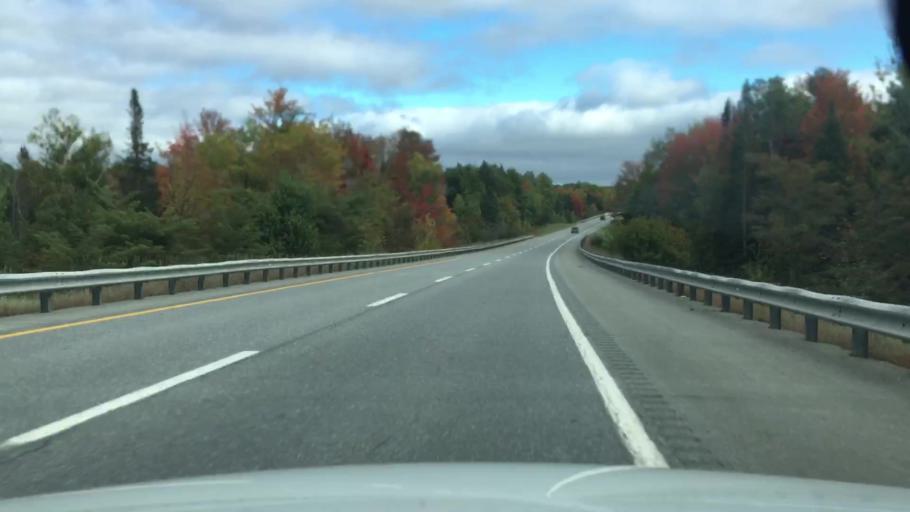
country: US
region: Maine
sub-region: Penobscot County
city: Carmel
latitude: 44.7706
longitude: -69.0031
